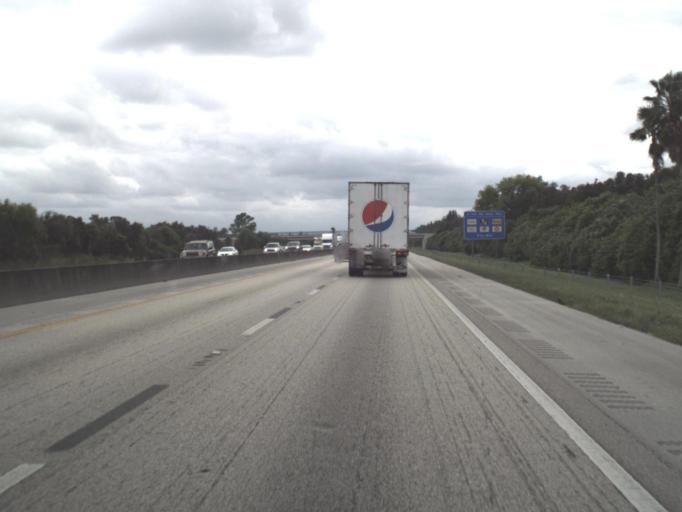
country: US
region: Florida
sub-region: Palm Beach County
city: Schall Circle
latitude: 26.7414
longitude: -80.1349
